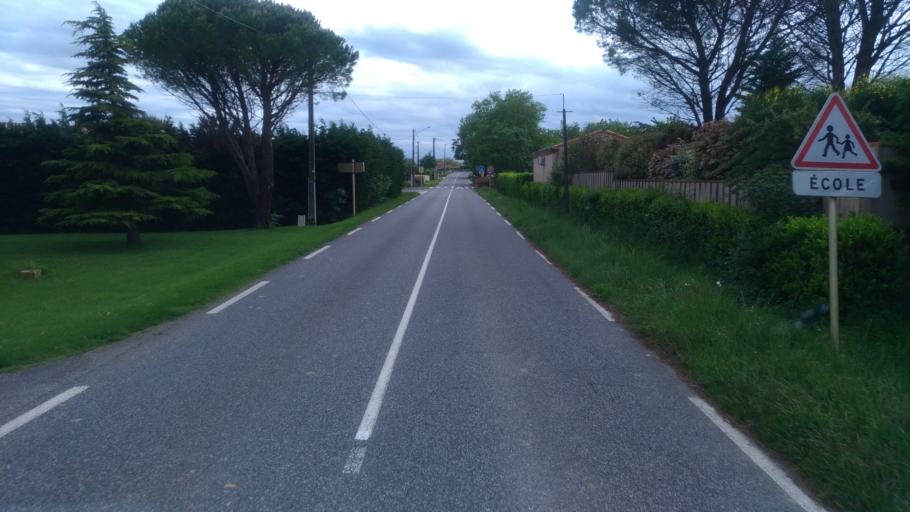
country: FR
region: Midi-Pyrenees
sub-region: Departement de la Haute-Garonne
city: Villefranche-de-Lauragais
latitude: 43.4240
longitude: 1.7505
